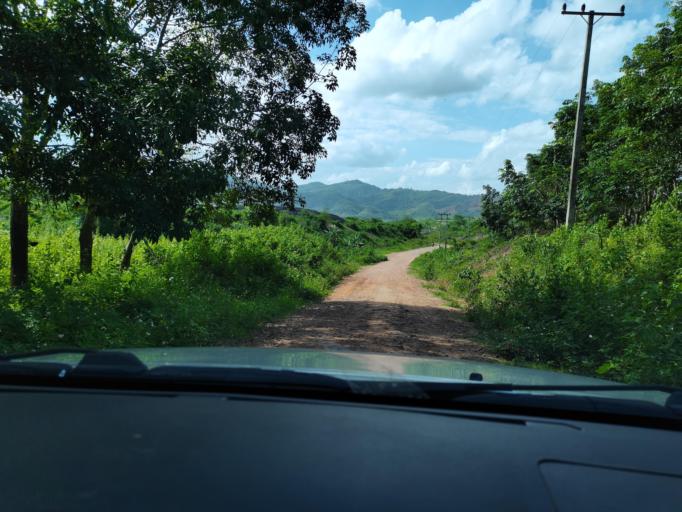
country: LA
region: Loungnamtha
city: Muang Nale
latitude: 20.5812
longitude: 101.0595
